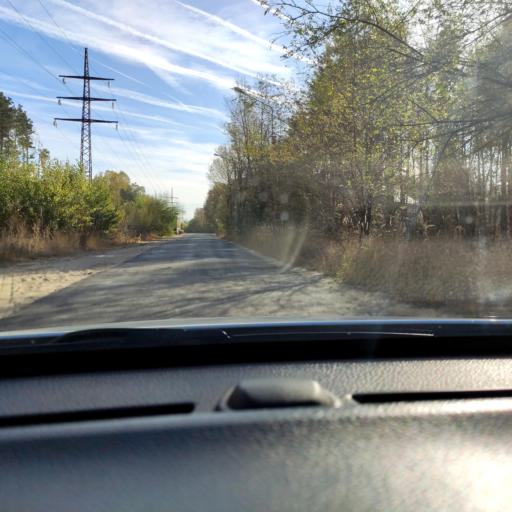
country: RU
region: Voronezj
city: Pridonskoy
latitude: 51.6841
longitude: 39.0950
